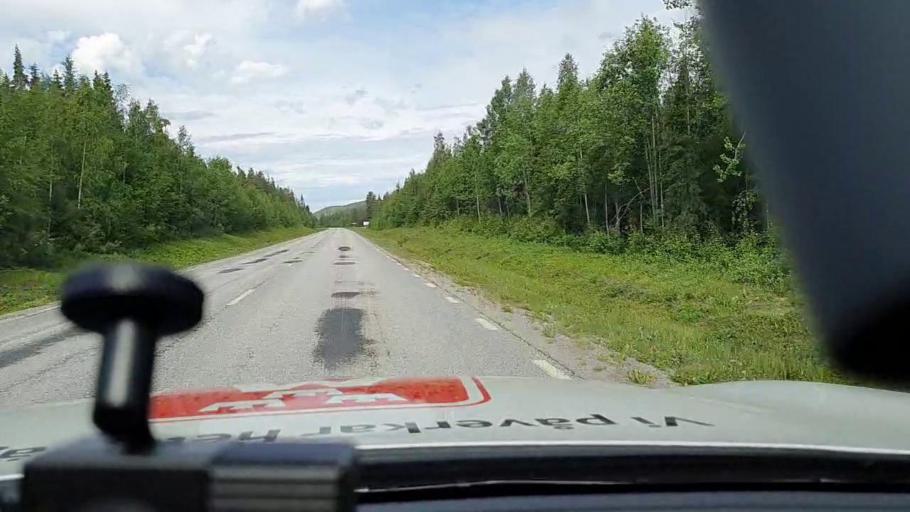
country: SE
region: Norrbotten
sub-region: Jokkmokks Kommun
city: Jokkmokk
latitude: 66.5505
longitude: 20.1215
